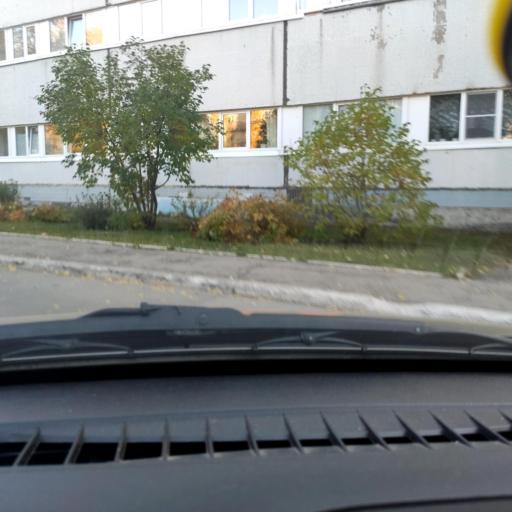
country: RU
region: Samara
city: Tol'yatti
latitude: 53.5222
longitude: 49.3300
